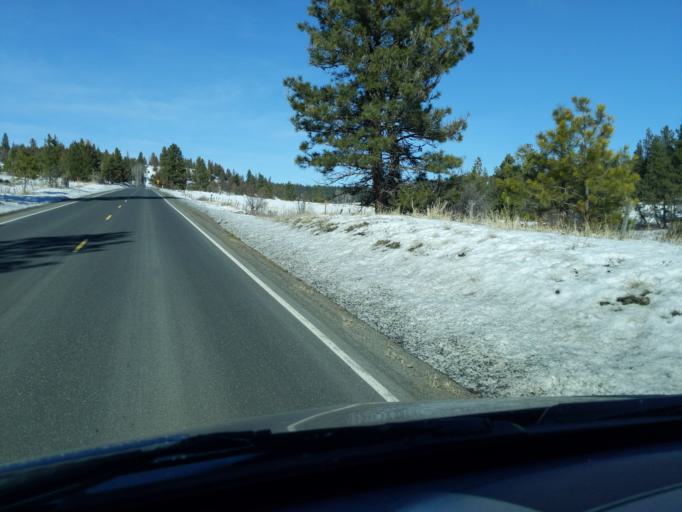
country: US
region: Oregon
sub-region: Grant County
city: John Day
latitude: 44.8987
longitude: -119.0141
